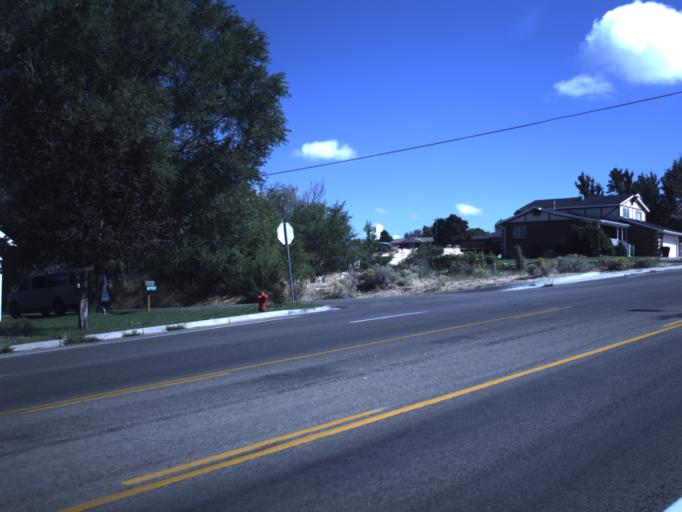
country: US
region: Utah
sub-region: Utah County
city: Payson
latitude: 40.0313
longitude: -111.7402
